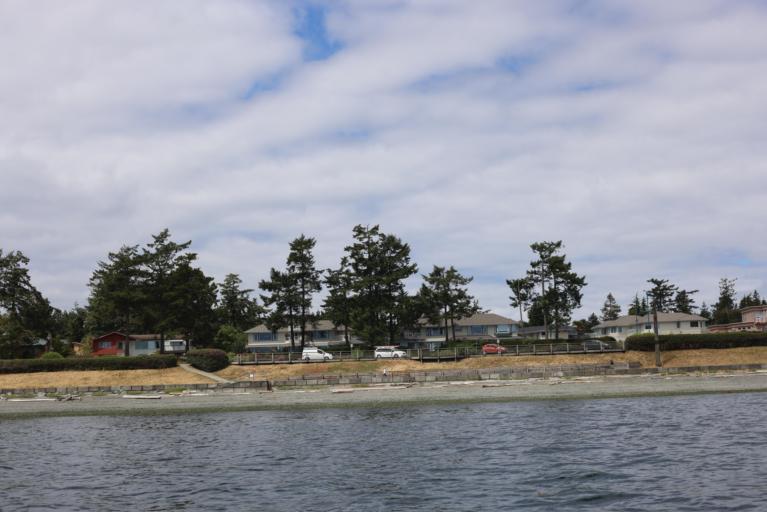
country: CA
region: British Columbia
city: North Saanich
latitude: 48.6368
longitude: -123.4019
